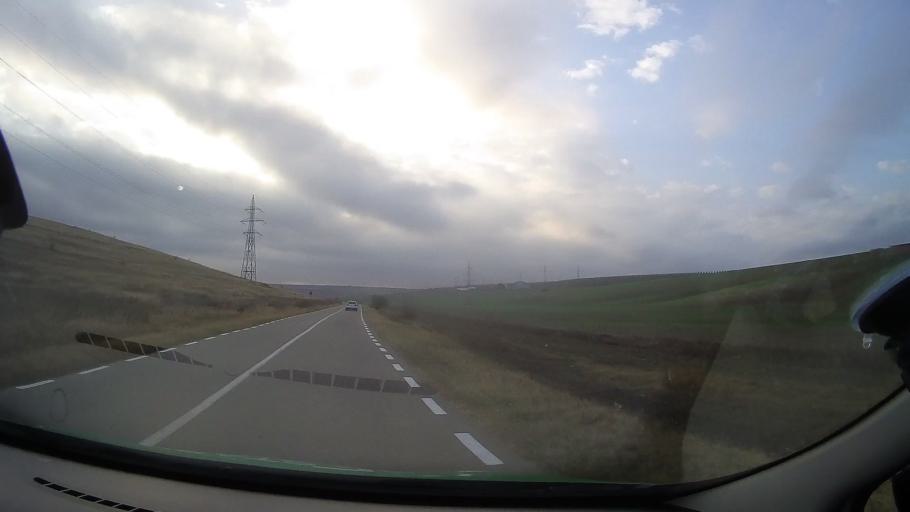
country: RO
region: Constanta
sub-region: Comuna Pestera
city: Pestera
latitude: 44.2017
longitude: 28.1430
